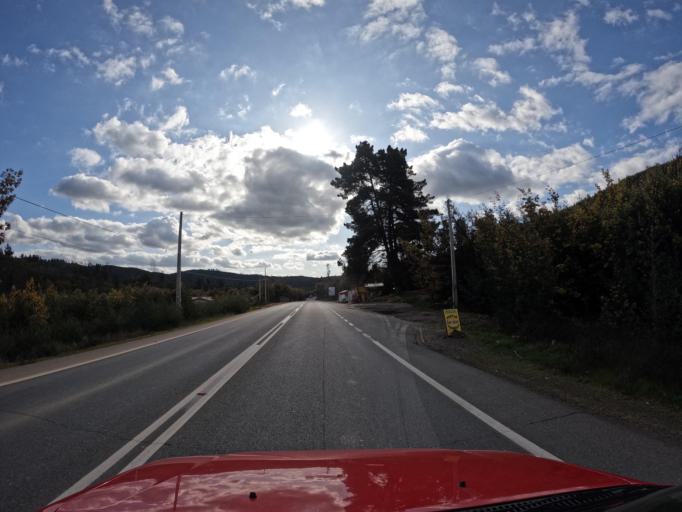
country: CL
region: Maule
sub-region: Provincia de Talca
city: Constitucion
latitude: -35.5355
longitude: -72.1673
